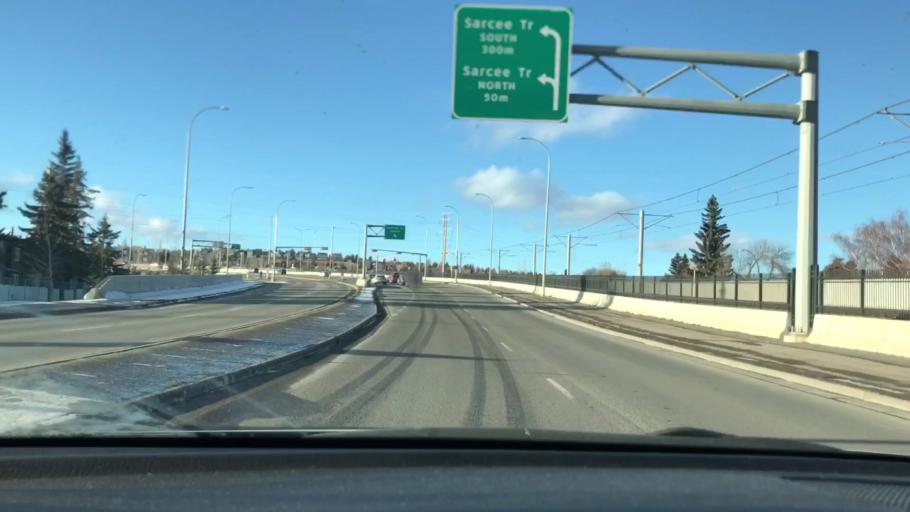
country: CA
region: Alberta
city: Calgary
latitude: 51.0386
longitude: -114.1602
